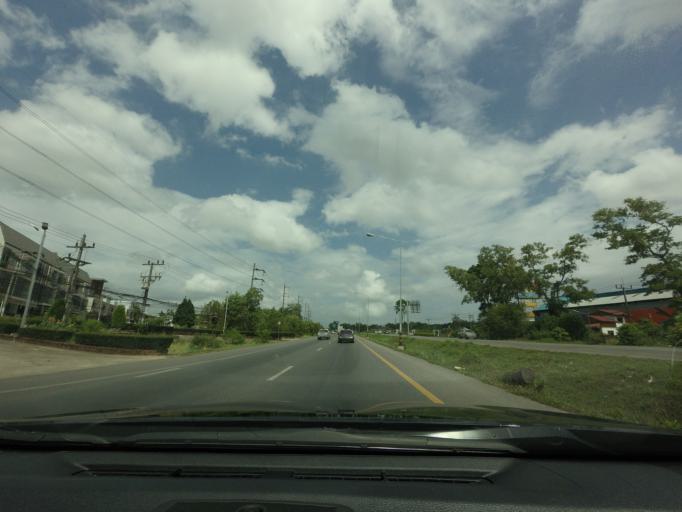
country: TH
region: Songkhla
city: Hat Yai
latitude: 6.9839
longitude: 100.4510
